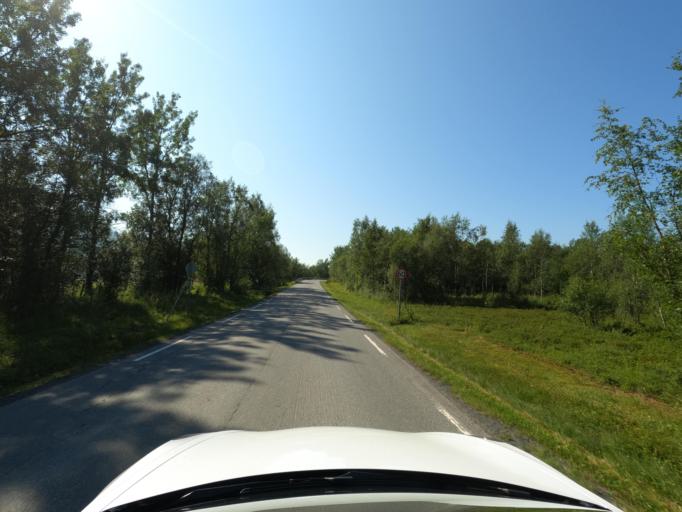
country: NO
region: Nordland
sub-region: Ballangen
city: Ballangen
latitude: 68.3588
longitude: 16.8752
